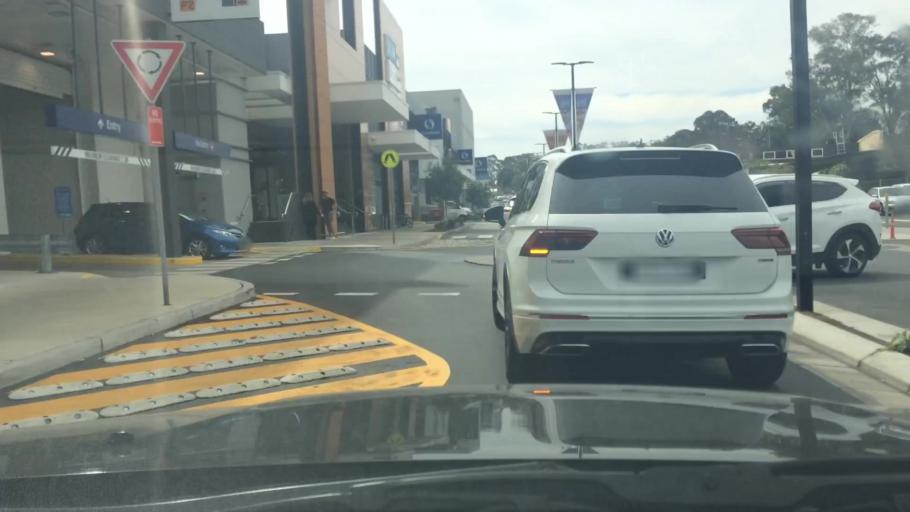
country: AU
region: New South Wales
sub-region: Fairfield
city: Cabramatta West
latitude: -33.8592
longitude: 150.8996
